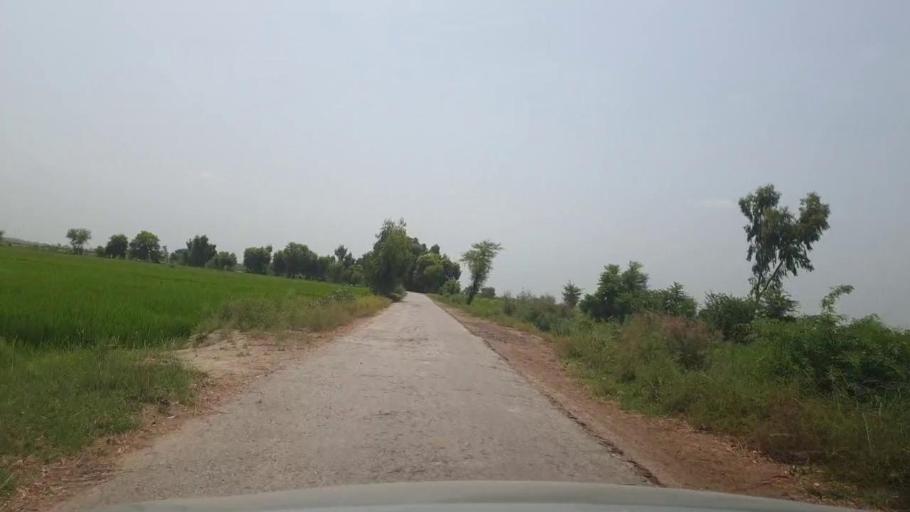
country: PK
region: Sindh
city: Garhi Yasin
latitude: 27.9439
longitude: 68.3757
